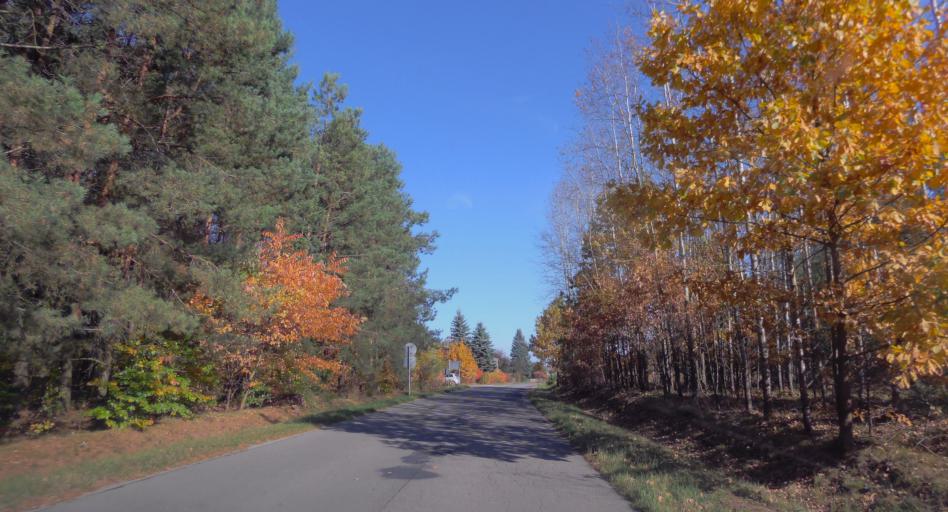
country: PL
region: Subcarpathian Voivodeship
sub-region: Powiat lezajski
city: Wola Zarczycka
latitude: 50.2612
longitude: 22.2400
